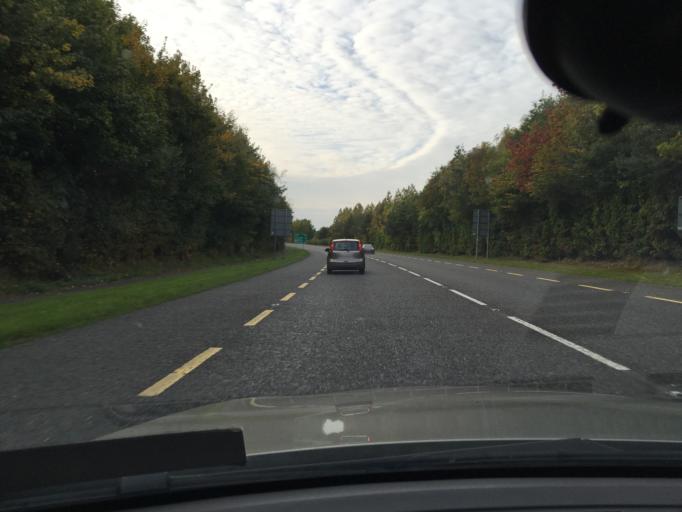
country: IE
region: Leinster
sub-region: An Longfort
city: Longford
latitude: 53.7400
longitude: -7.7806
